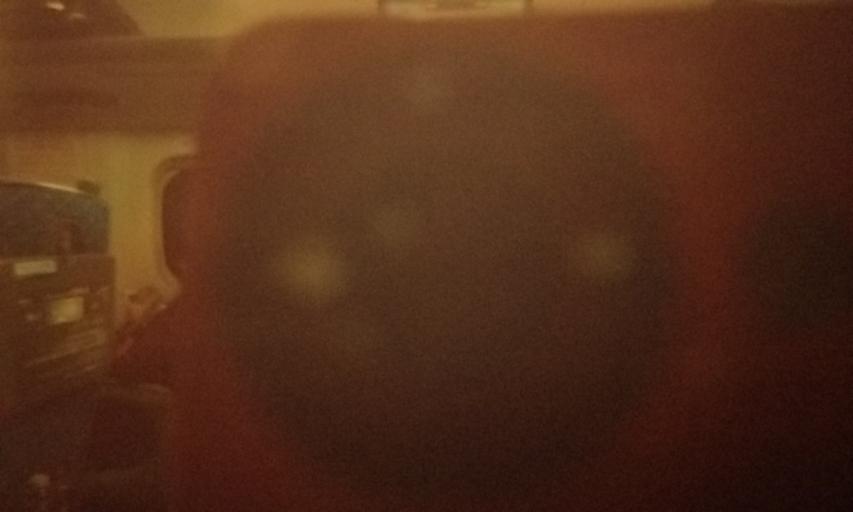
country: JP
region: Shizuoka
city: Kanaya
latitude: 34.7839
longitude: 138.1372
